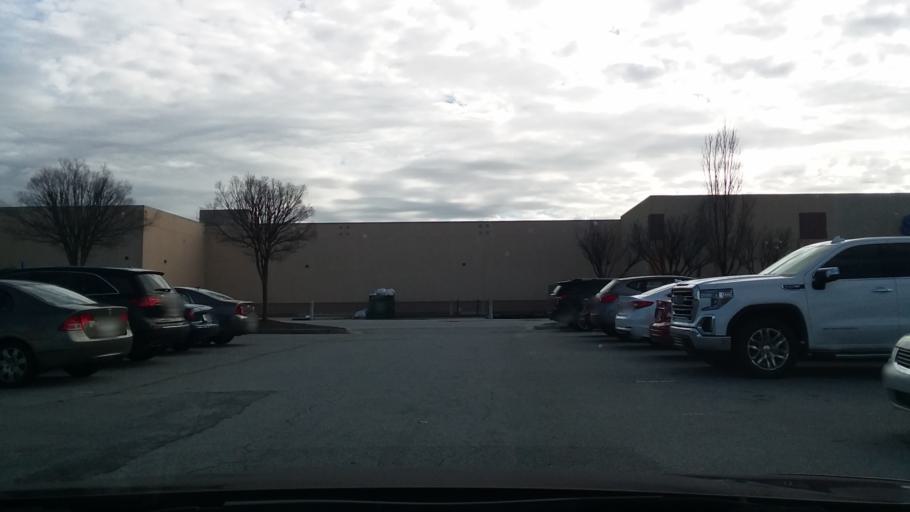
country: US
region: Georgia
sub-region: Gwinnett County
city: Duluth
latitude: 33.9819
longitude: -84.0821
